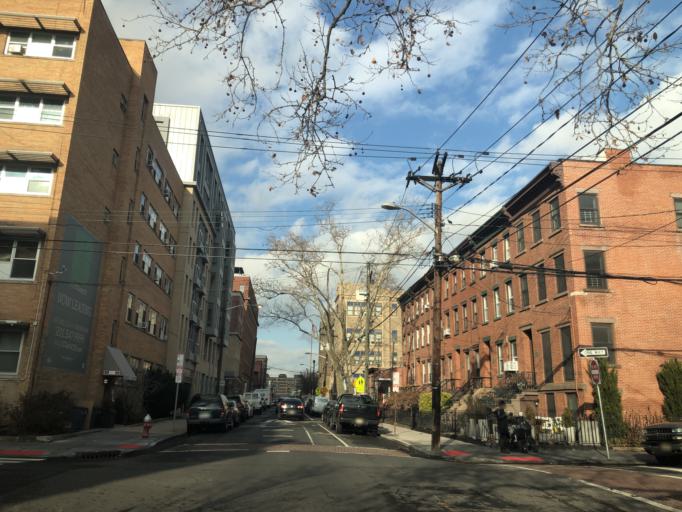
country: US
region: New Jersey
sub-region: Hudson County
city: Hoboken
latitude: 40.7267
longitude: -74.0435
